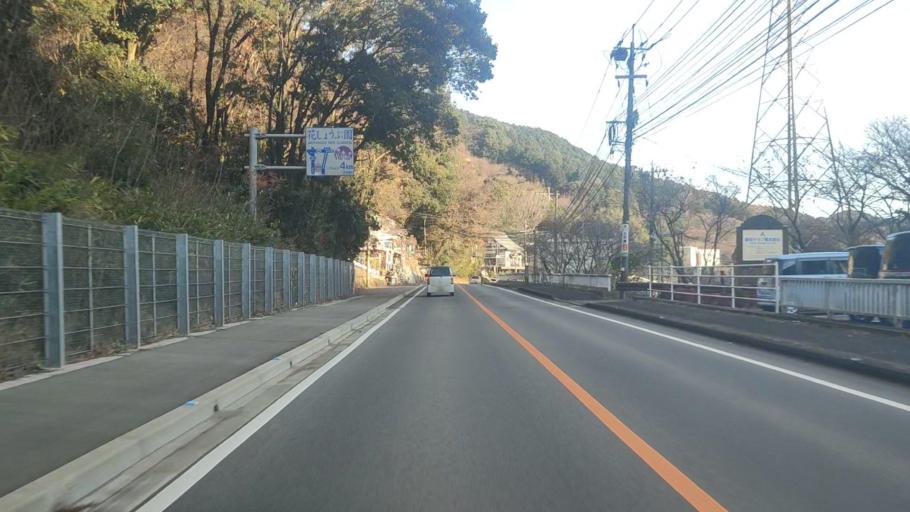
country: JP
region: Saga Prefecture
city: Saga-shi
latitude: 33.3318
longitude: 130.2649
